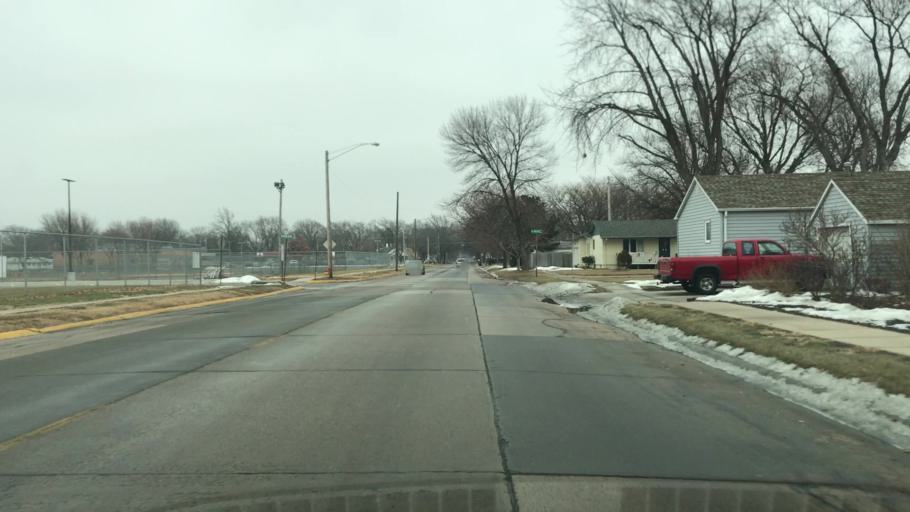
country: US
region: Nebraska
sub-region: Hall County
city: Grand Island
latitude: 40.9385
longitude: -98.3675
